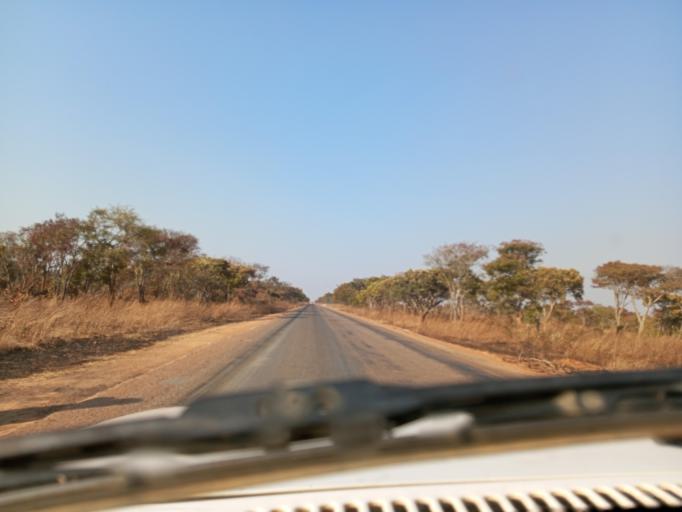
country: ZM
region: Northern
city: Mpika
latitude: -12.4041
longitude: 31.0872
